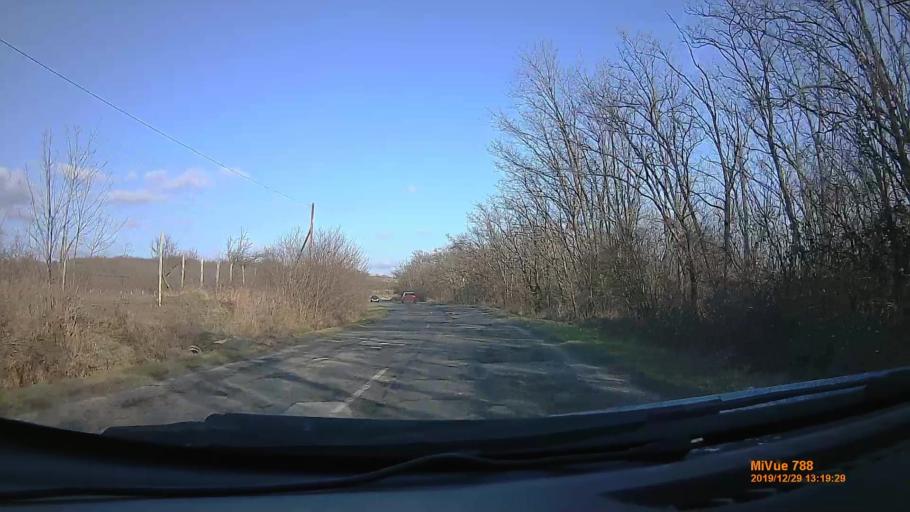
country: HU
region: Heves
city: Domoszlo
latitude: 47.8458
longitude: 20.1322
